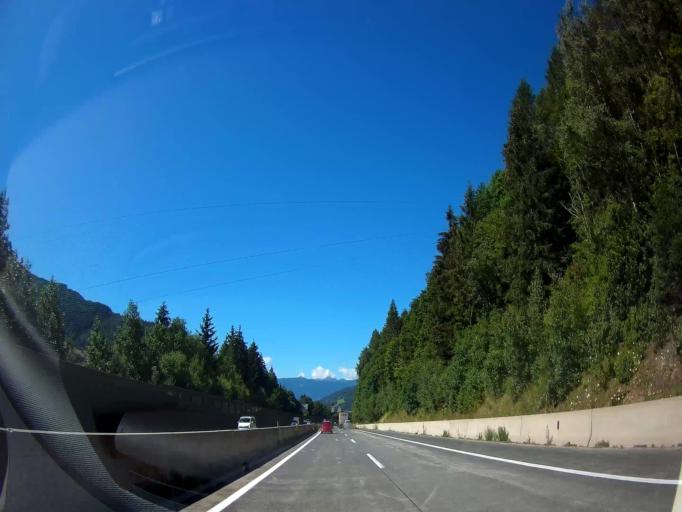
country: AT
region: Carinthia
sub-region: Politischer Bezirk Spittal an der Drau
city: Gmuend
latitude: 46.8971
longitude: 13.5265
